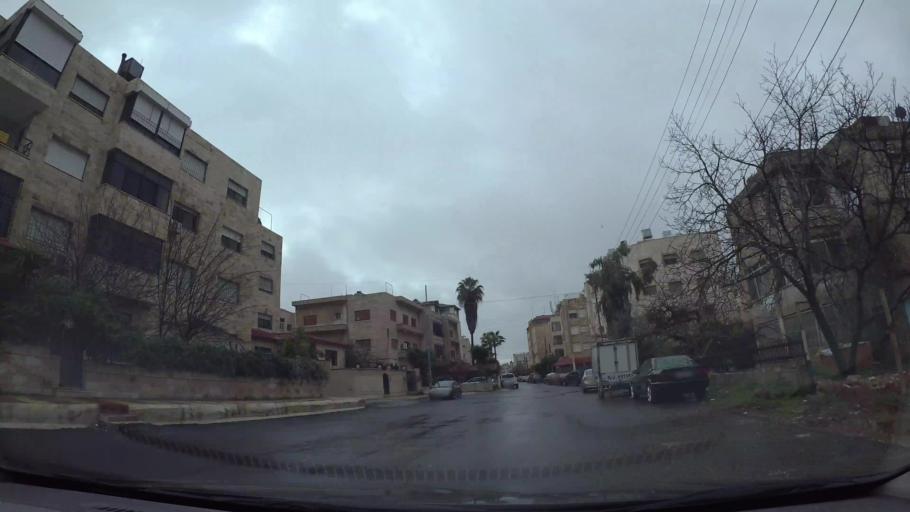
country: JO
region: Amman
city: Wadi as Sir
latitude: 31.9630
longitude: 35.8614
